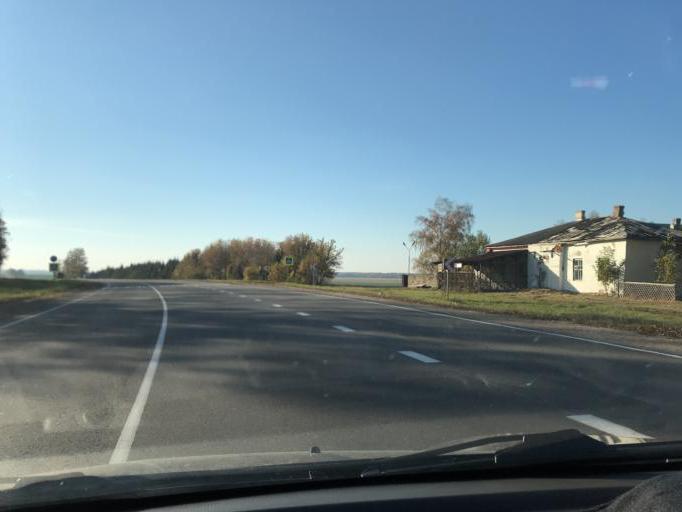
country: BY
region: Minsk
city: Urechcha
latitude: 53.0752
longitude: 27.7565
